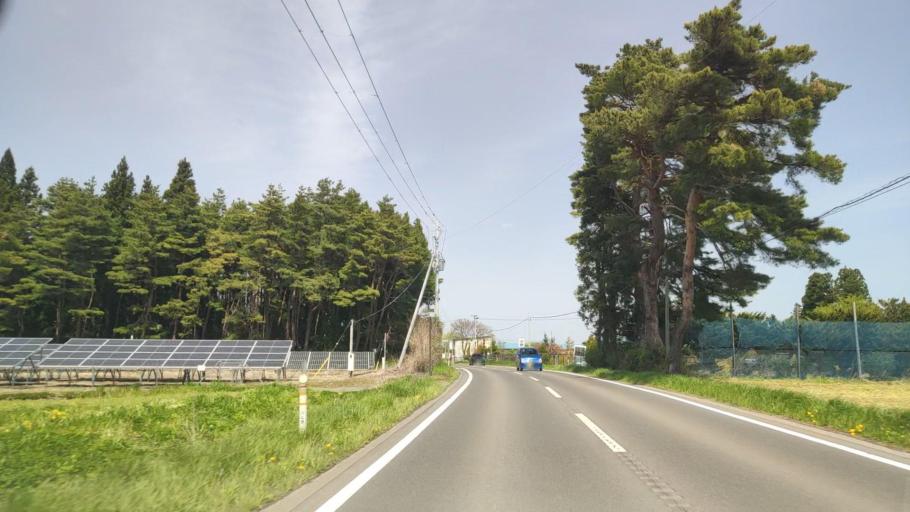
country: JP
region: Aomori
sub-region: Hachinohe Shi
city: Uchimaru
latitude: 40.5358
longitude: 141.4022
